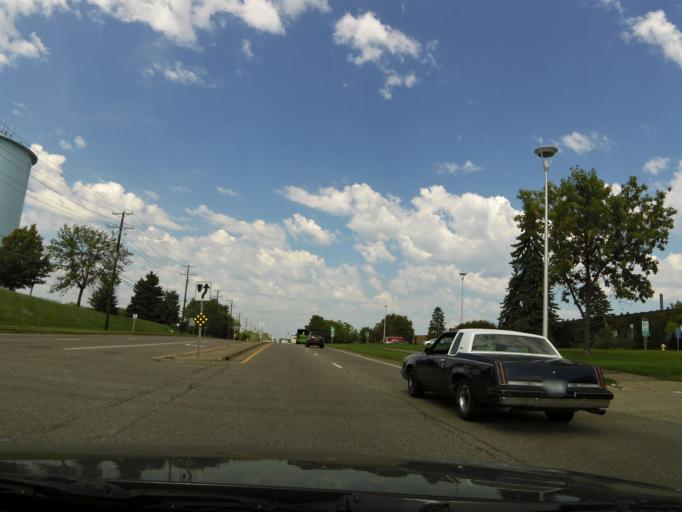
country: US
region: Minnesota
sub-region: Ramsey County
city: Maplewood
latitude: 44.9521
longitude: -93.0049
